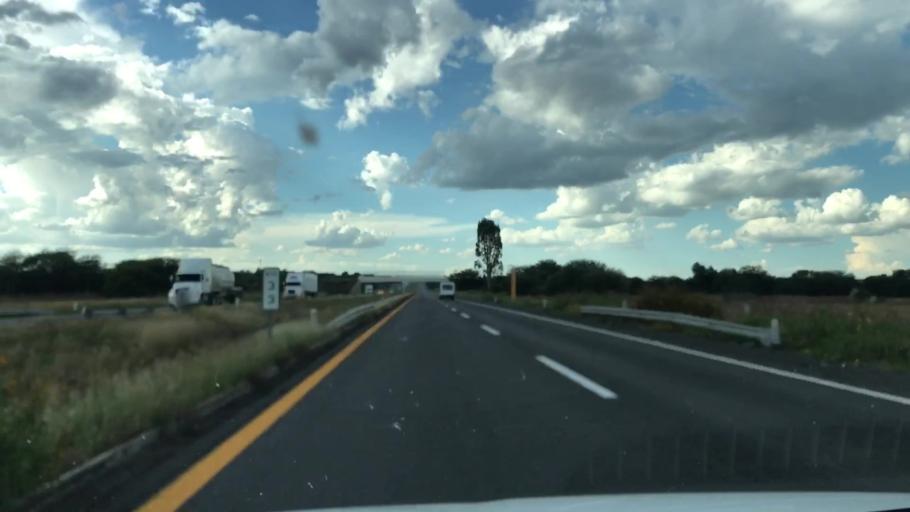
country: MX
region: Guanajuato
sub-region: Purisima del Rincon
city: Potrerillos (Guanajal)
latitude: 21.1581
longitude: -101.8536
